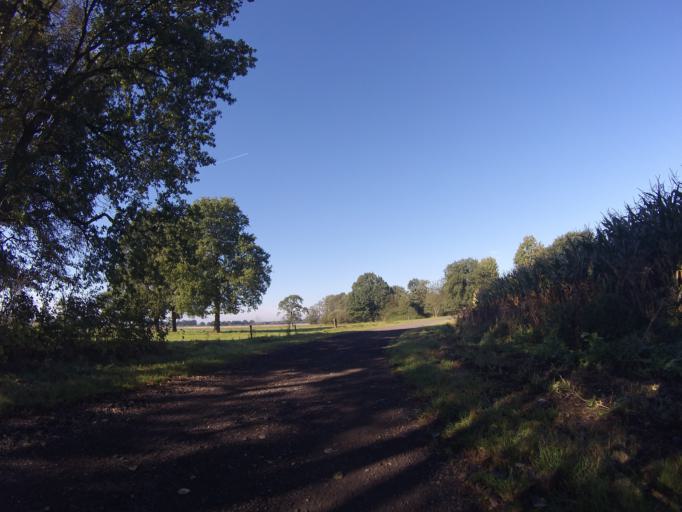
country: NL
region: Drenthe
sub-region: Gemeente Coevorden
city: Dalen
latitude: 52.7374
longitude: 6.6586
